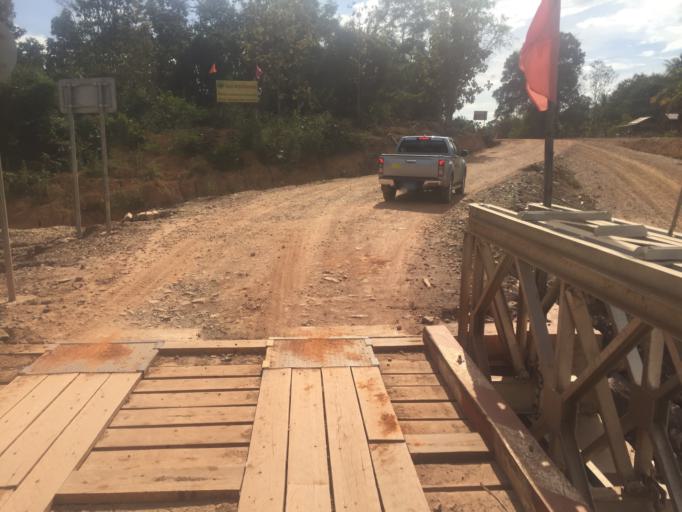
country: LA
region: Attapu
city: Attapu
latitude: 14.7977
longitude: 106.7547
